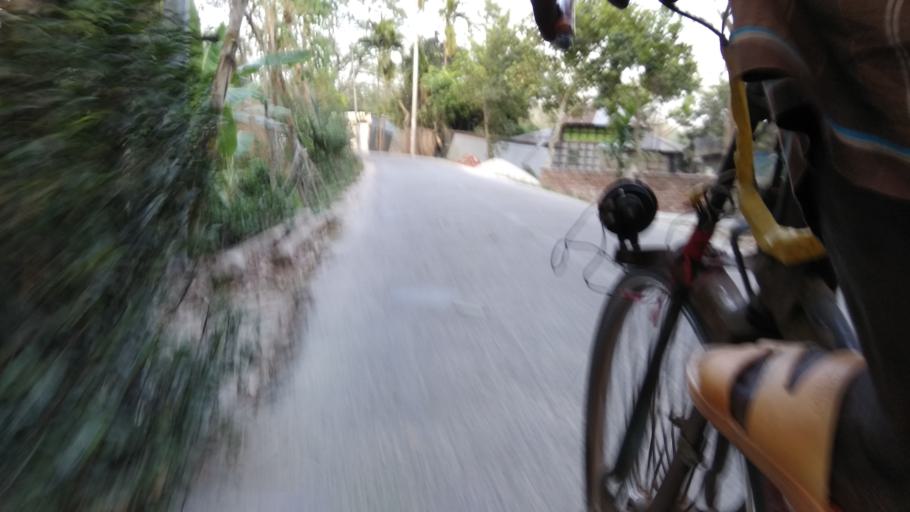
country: BD
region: Barisal
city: Mehendiganj
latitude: 22.9388
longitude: 90.4085
